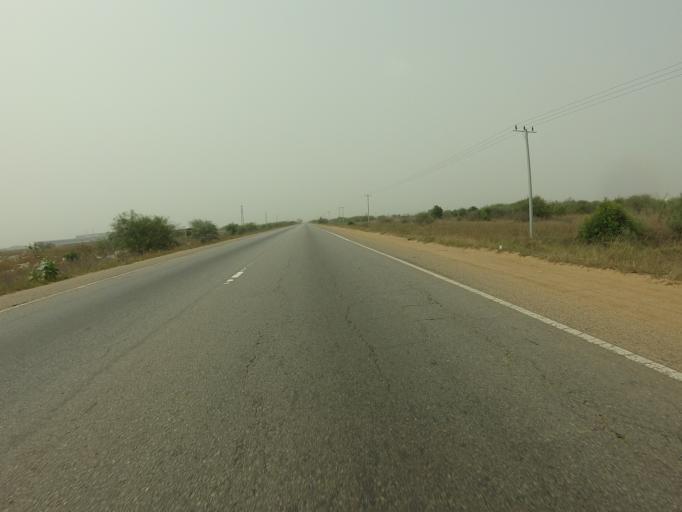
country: GH
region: Greater Accra
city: Tema
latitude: 5.8292
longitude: 0.2044
